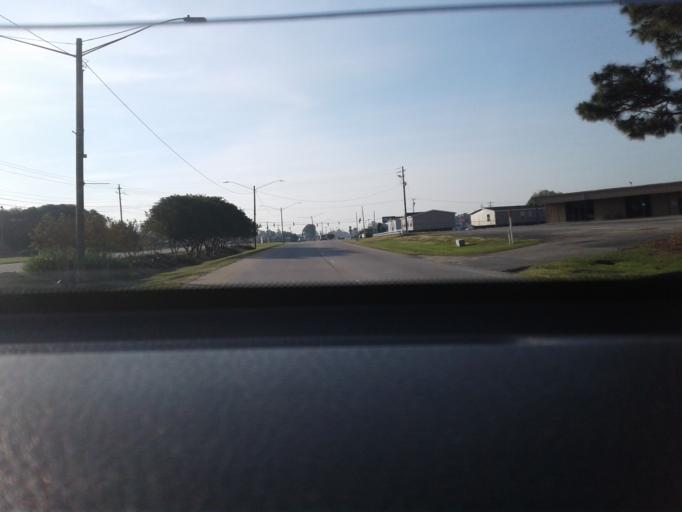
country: US
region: North Carolina
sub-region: Harnett County
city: Dunn
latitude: 35.3197
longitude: -78.6327
